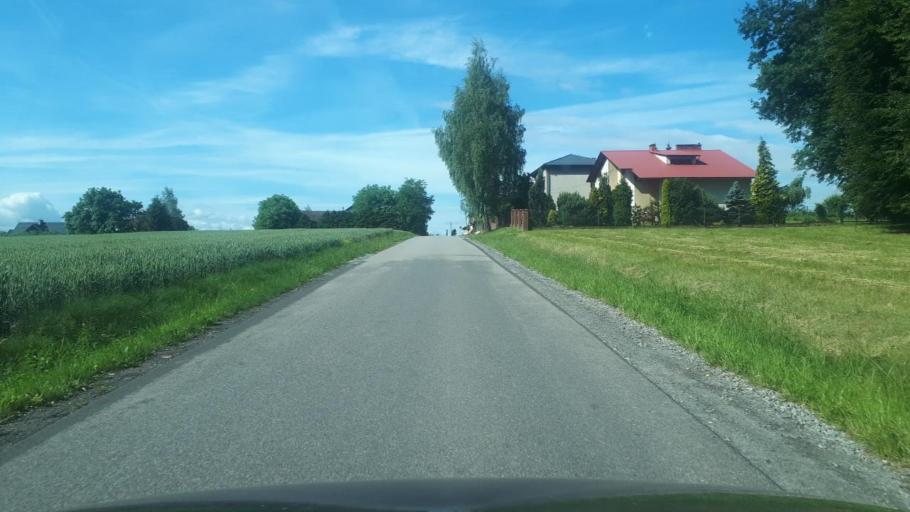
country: PL
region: Silesian Voivodeship
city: Janowice
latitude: 49.8966
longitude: 19.1082
